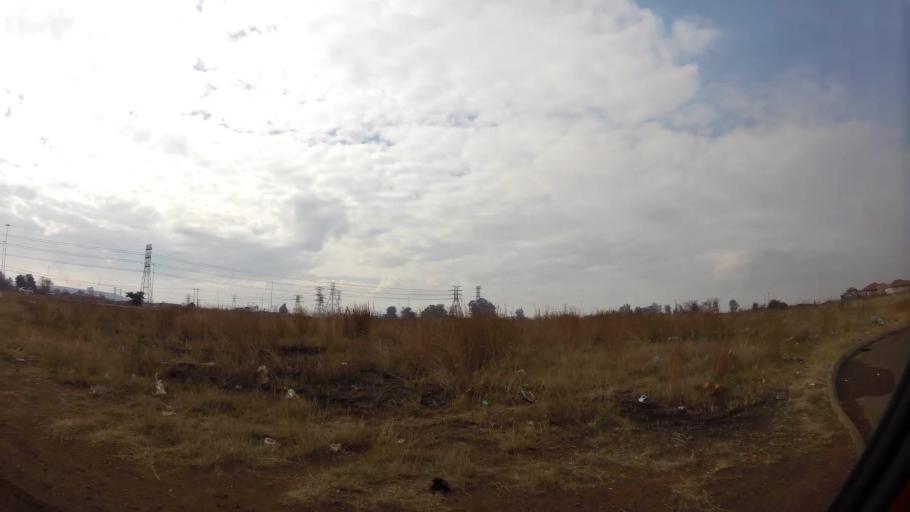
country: ZA
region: Gauteng
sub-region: Sedibeng District Municipality
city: Vanderbijlpark
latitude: -26.6815
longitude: 27.8494
